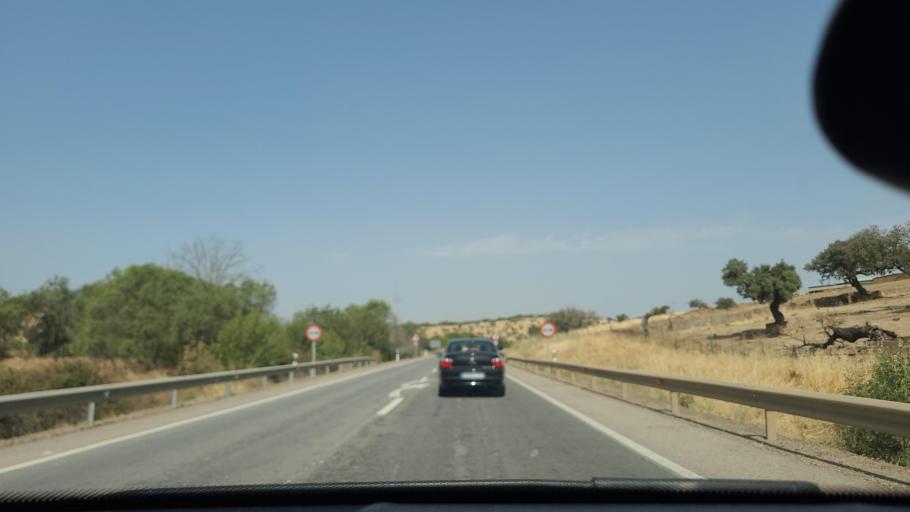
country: ES
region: Extremadura
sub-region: Provincia de Badajoz
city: Zafra
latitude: 38.4592
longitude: -6.4367
